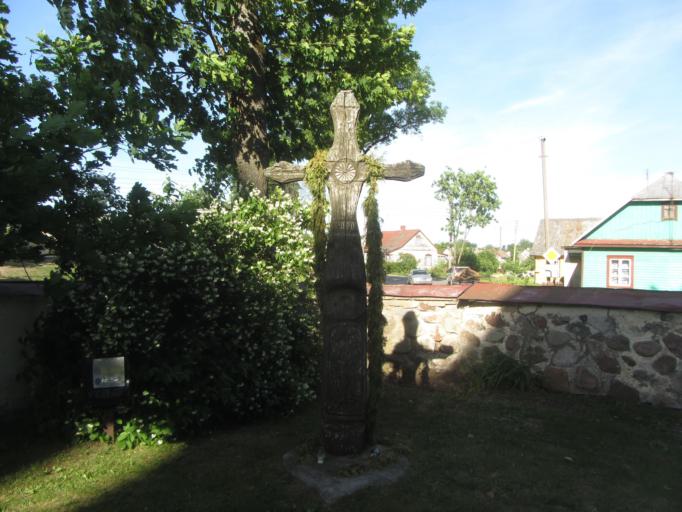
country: LT
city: Jieznas
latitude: 54.5995
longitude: 24.1745
